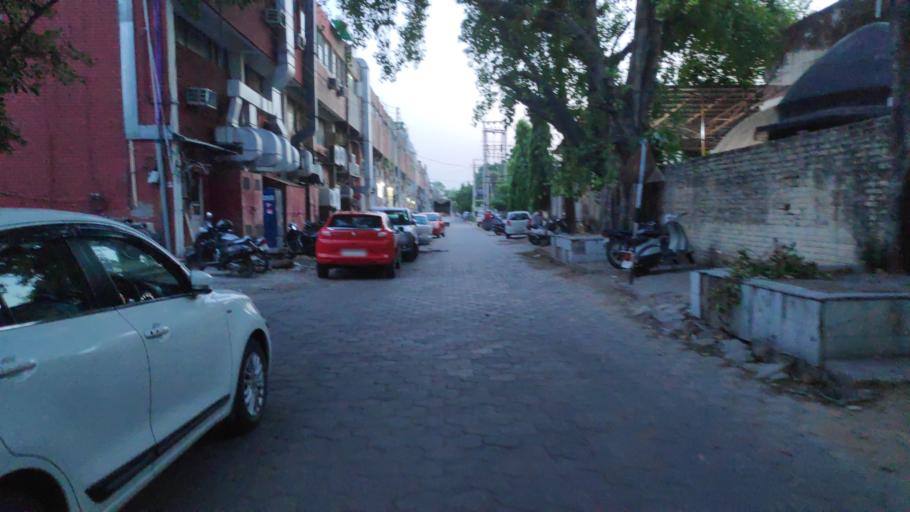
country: IN
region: Chandigarh
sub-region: Chandigarh
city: Chandigarh
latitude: 30.7232
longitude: 76.7623
